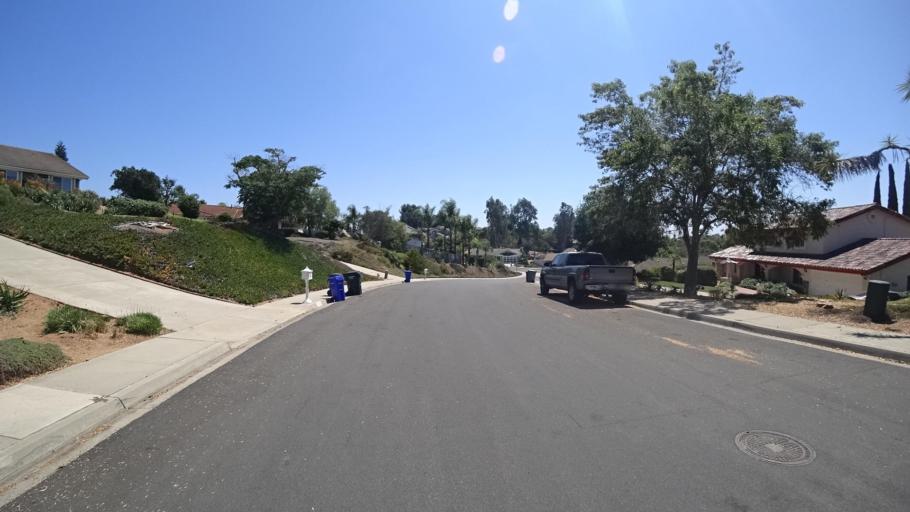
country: US
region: California
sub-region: San Diego County
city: Fallbrook
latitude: 33.3643
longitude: -117.2566
